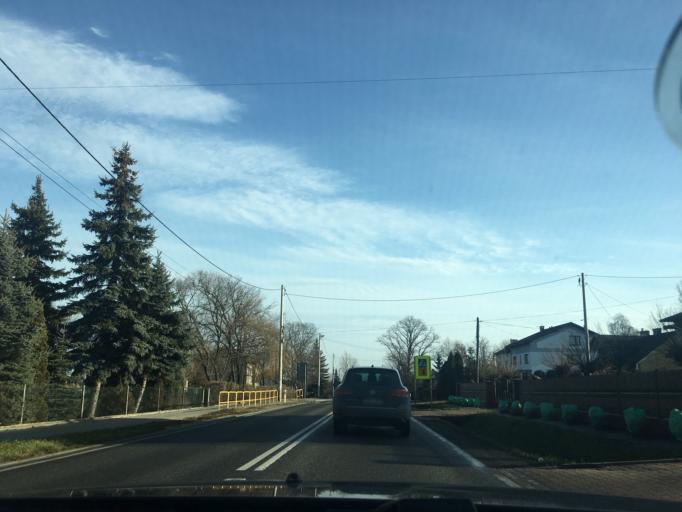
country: PL
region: Swietokrzyskie
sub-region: Powiat jedrzejowski
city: Jedrzejow
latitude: 50.6307
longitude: 20.3312
